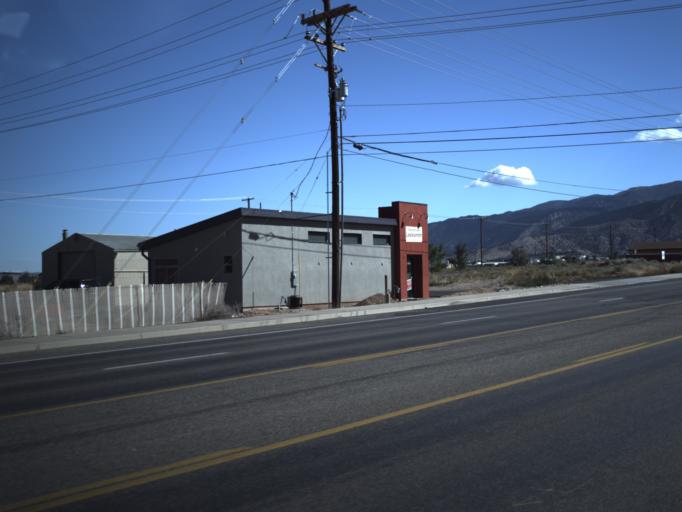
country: US
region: Utah
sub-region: Iron County
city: Cedar City
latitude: 37.6850
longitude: -113.1025
